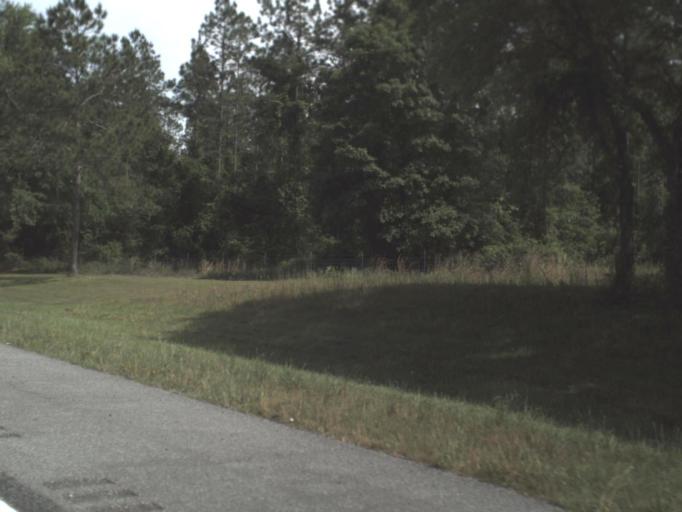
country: US
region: Florida
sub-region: Suwannee County
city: Wellborn
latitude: 30.2757
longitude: -82.8058
